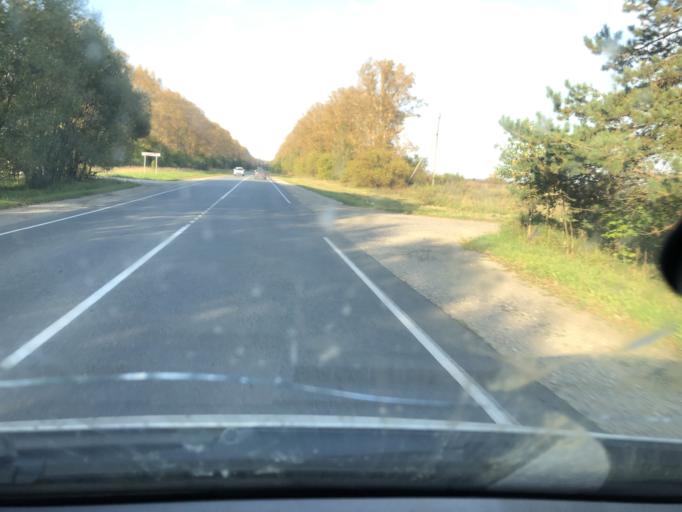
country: RU
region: Kaluga
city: Peremyshl'
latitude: 54.2345
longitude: 36.0643
